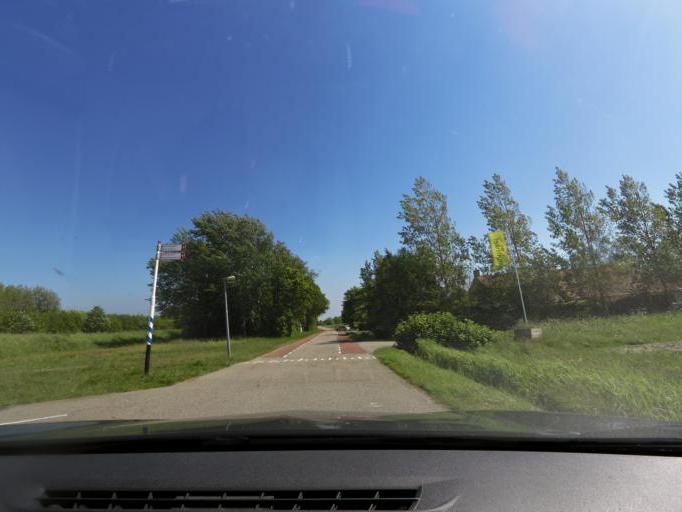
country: NL
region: South Holland
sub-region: Gemeente Goeree-Overflakkee
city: Goedereede
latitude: 51.8042
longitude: 4.0107
